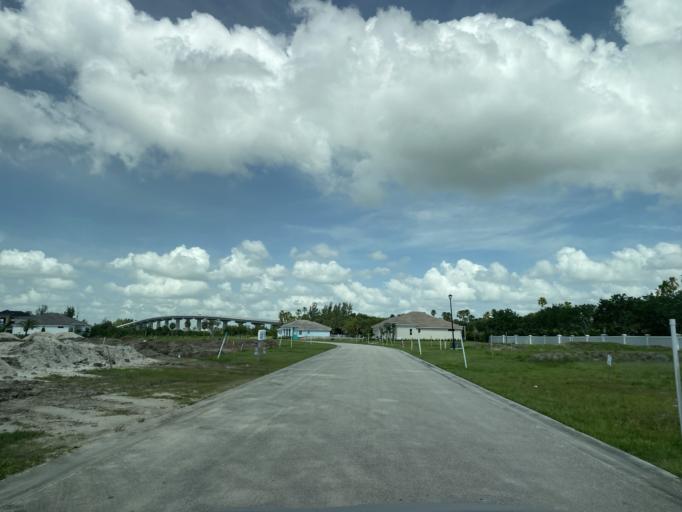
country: US
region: Florida
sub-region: Indian River County
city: Wabasso Beach
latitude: 27.7629
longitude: -80.4108
